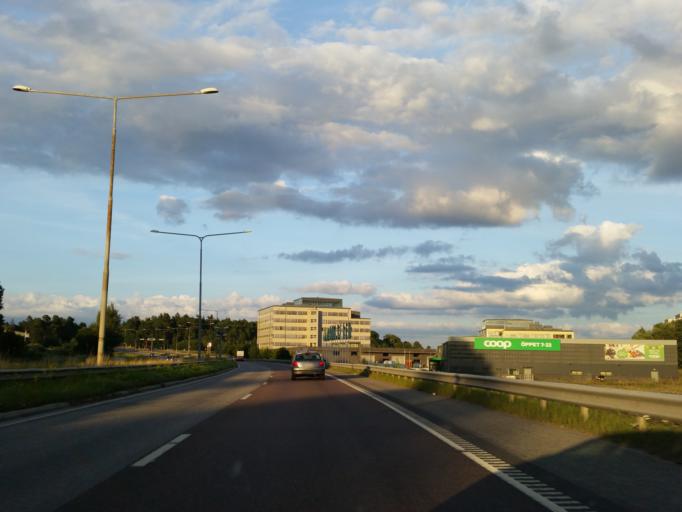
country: SE
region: Stockholm
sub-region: Sundbybergs Kommun
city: Sundbyberg
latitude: 59.3794
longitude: 17.9616
